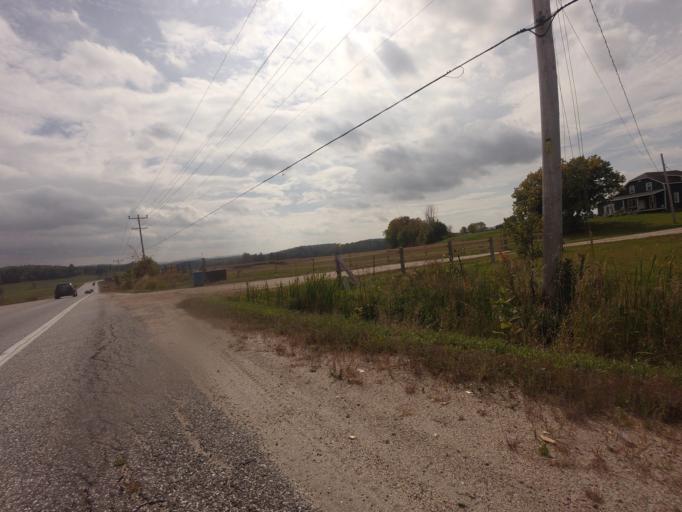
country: CA
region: Quebec
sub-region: Outaouais
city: Wakefield
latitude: 45.8557
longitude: -76.0042
